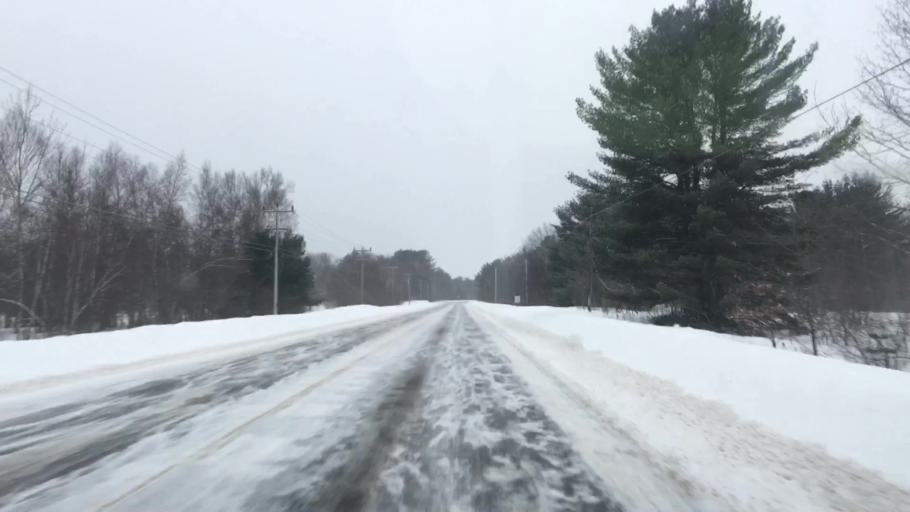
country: US
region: Maine
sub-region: Penobscot County
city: Medway
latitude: 45.5620
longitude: -68.3934
